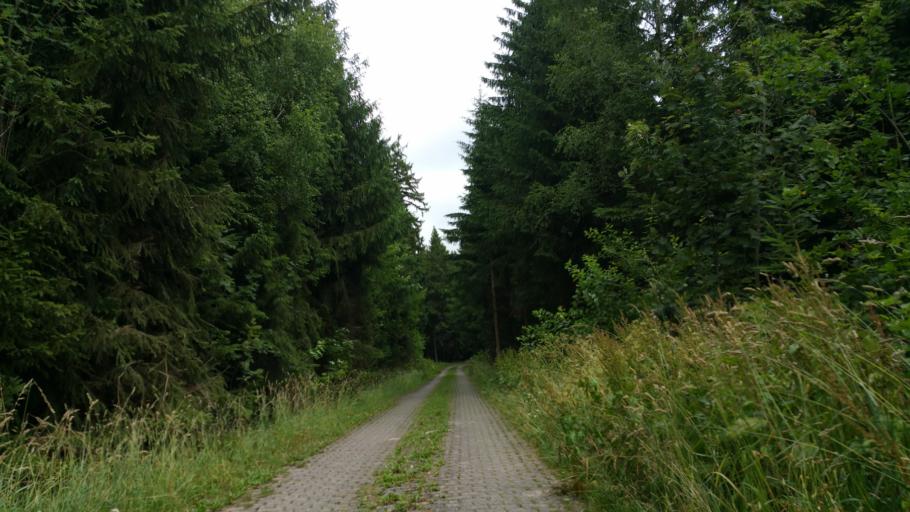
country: DE
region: Bavaria
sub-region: Upper Franconia
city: Schwarzenbach an der Saale
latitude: 50.2295
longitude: 11.9758
